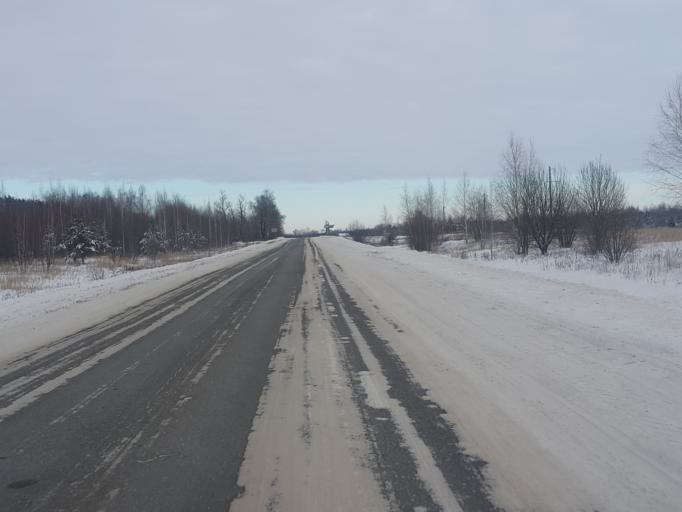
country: RU
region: Tambov
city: Platonovka
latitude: 52.8674
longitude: 41.8574
